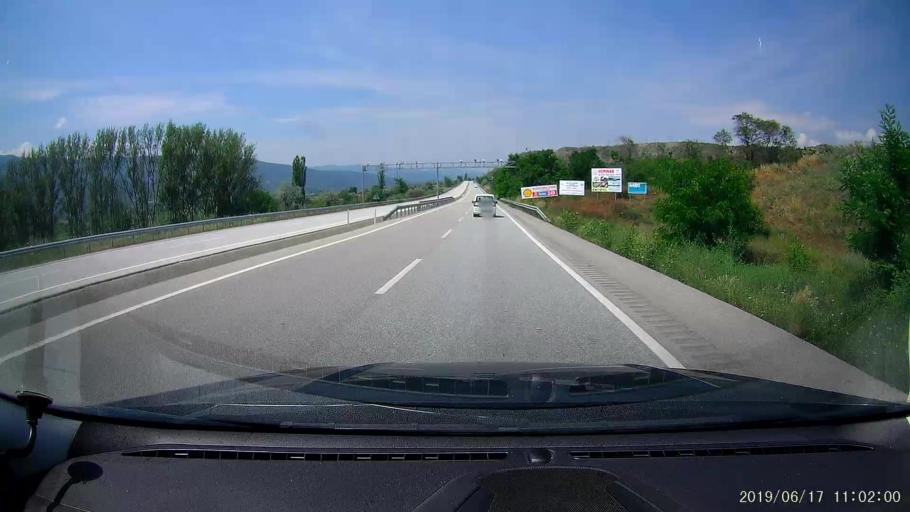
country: TR
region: Kastamonu
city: Tosya
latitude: 41.0226
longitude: 34.1447
